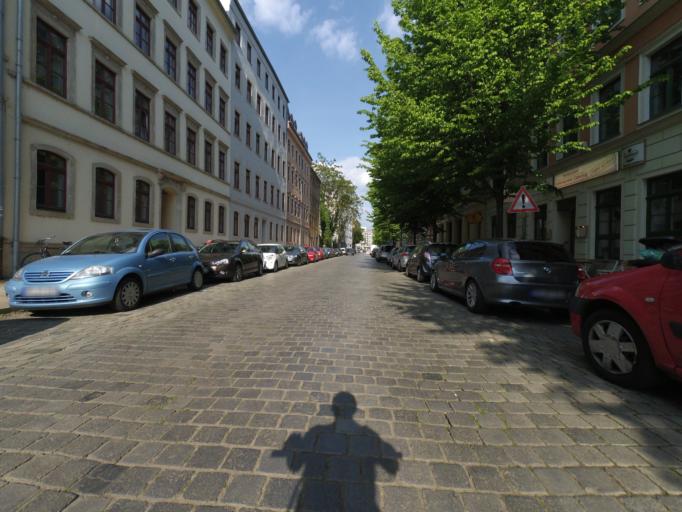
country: DE
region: Saxony
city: Dresden
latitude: 51.0535
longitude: 13.7253
